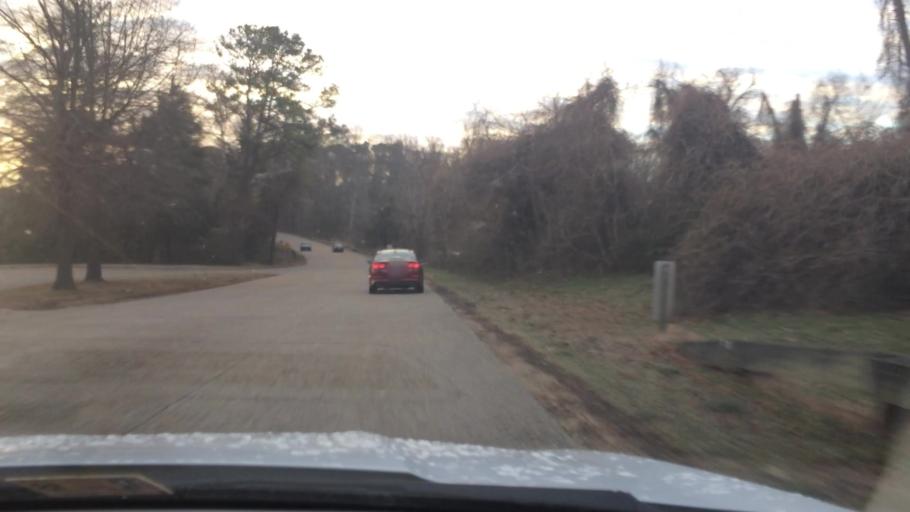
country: US
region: Virginia
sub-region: York County
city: Yorktown
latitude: 37.2542
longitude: -76.5409
